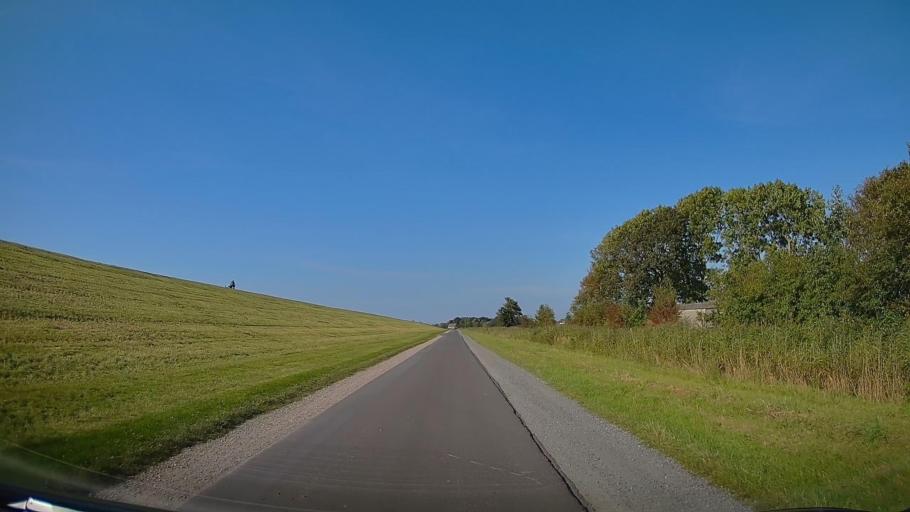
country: DE
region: Lower Saxony
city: Wremen
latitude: 53.6509
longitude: 8.4948
